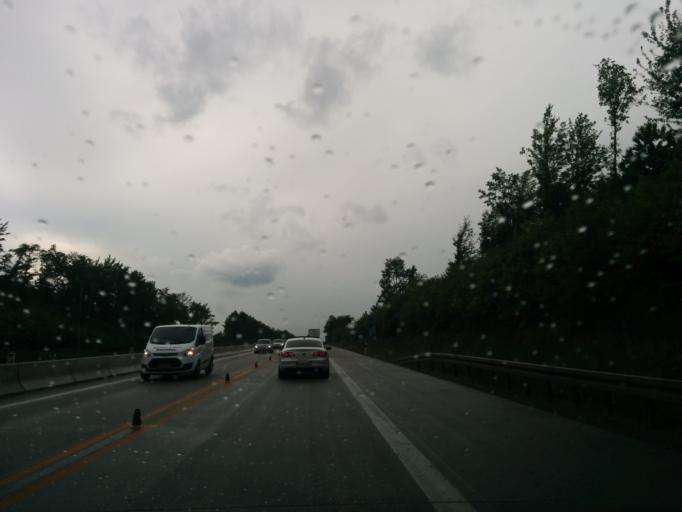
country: DE
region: Bavaria
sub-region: Regierungsbezirk Unterfranken
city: Obernbreit
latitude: 49.6475
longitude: 10.1542
